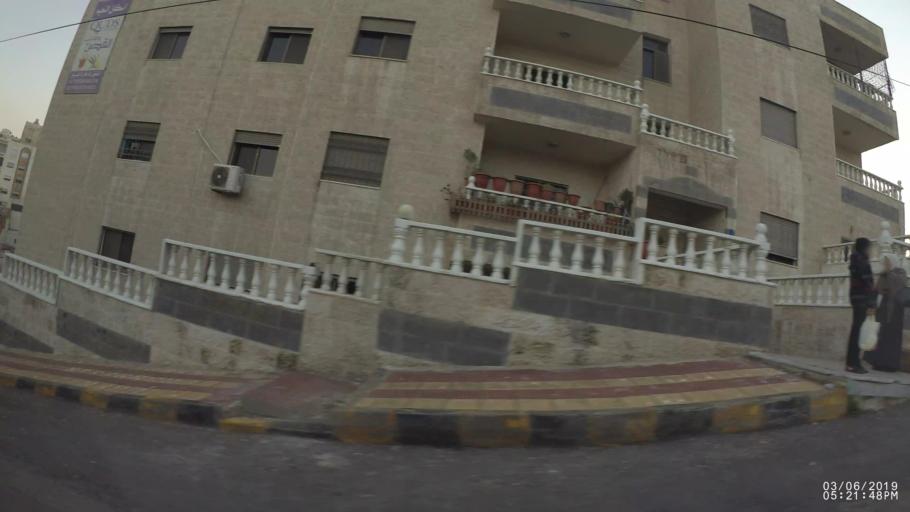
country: JO
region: Amman
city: Amman
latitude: 31.9924
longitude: 35.9558
